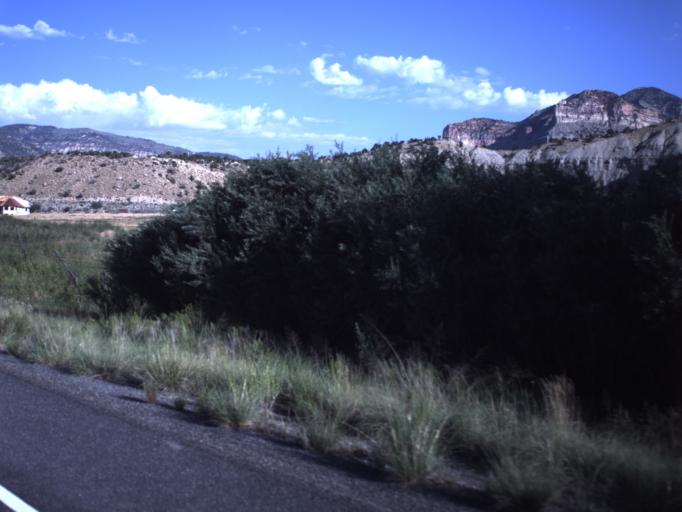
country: US
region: Utah
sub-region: Emery County
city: Huntington
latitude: 39.3622
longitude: -111.0377
